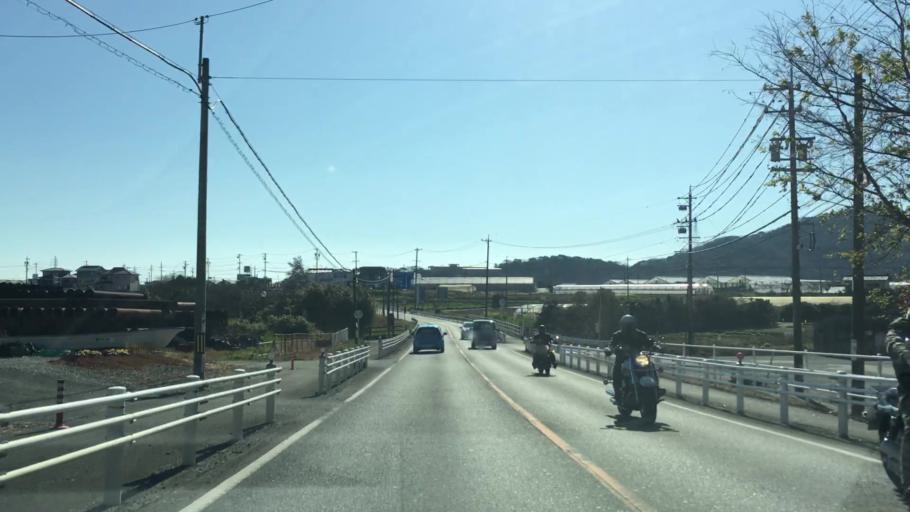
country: JP
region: Aichi
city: Tahara
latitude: 34.6955
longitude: 137.2773
